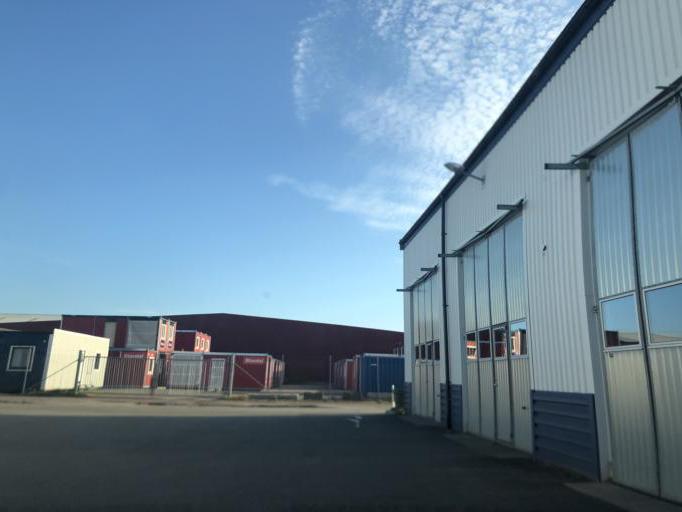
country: SE
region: Vaestra Goetaland
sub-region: Goteborg
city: Eriksbo
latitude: 57.7462
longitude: 12.0003
